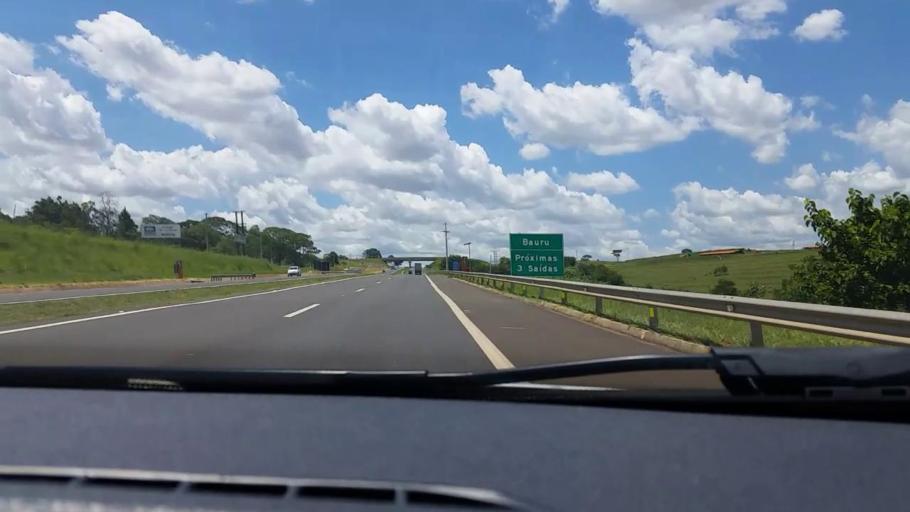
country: BR
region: Sao Paulo
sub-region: Bauru
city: Bauru
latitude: -22.4031
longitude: -49.0932
